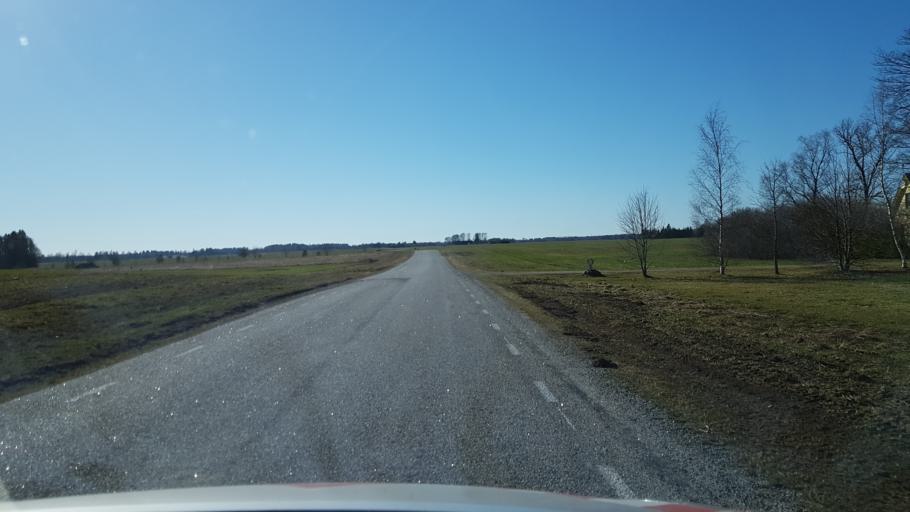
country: EE
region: Laeaene-Virumaa
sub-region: Haljala vald
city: Haljala
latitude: 59.4345
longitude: 26.2284
